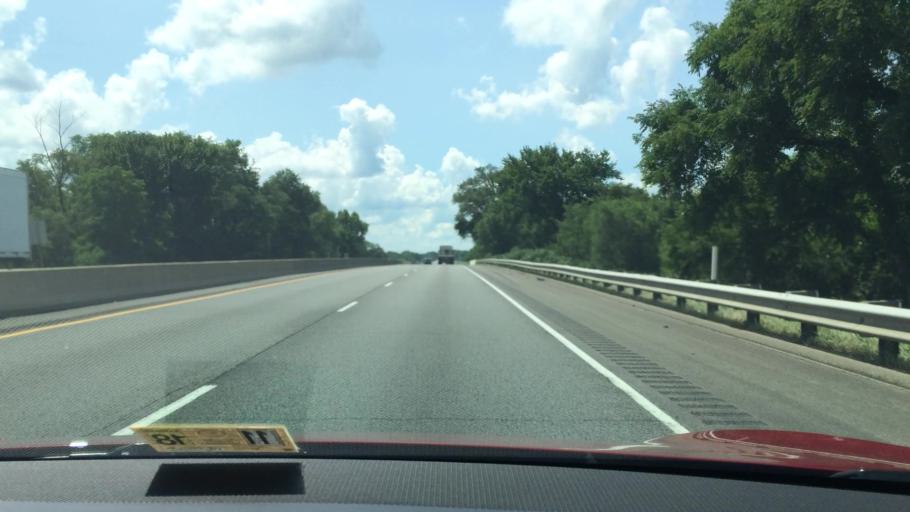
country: US
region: Indiana
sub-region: Saint Joseph County
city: South Bend
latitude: 41.6805
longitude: -86.3410
